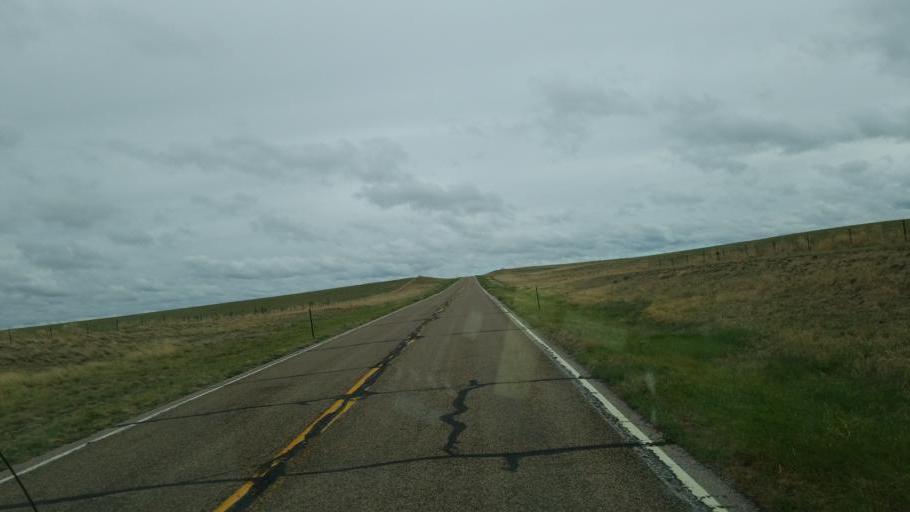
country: US
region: Colorado
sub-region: Lincoln County
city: Hugo
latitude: 38.8503
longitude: -103.4479
